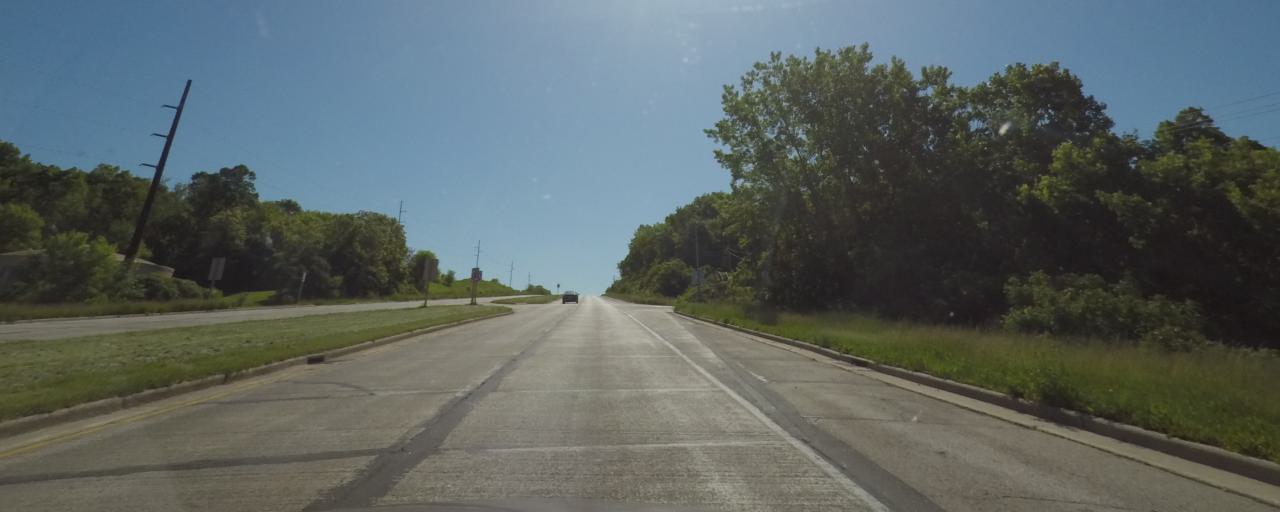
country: US
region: Wisconsin
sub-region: Fond du Lac County
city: Fond du Lac
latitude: 43.7838
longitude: -88.3842
